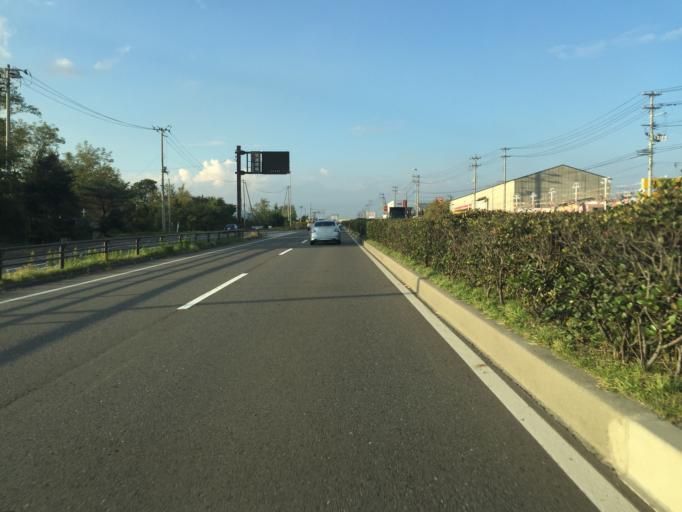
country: JP
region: Fukushima
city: Koriyama
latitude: 37.4557
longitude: 140.3783
